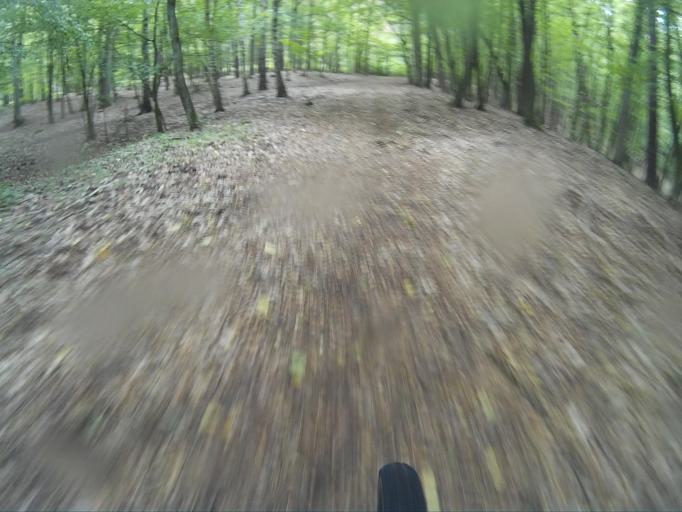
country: PL
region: Kujawsko-Pomorskie
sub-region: Powiat tucholski
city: Tuchola
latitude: 53.5803
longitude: 17.9103
